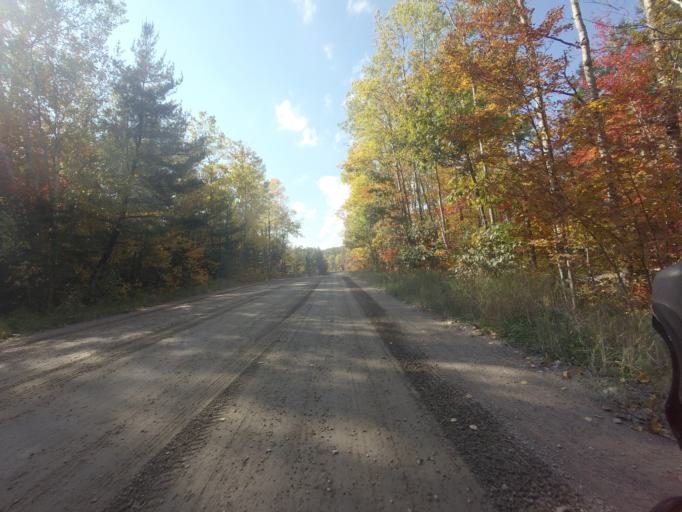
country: CA
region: Ontario
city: Petawawa
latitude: 45.8214
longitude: -77.4411
